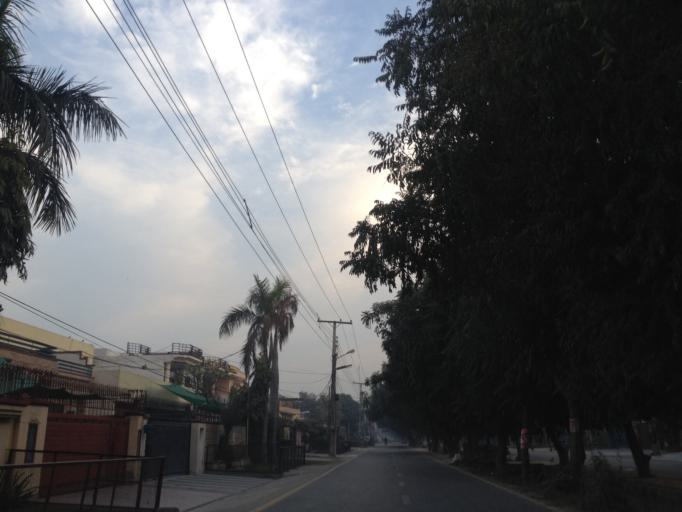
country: PK
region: Punjab
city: Lahore
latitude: 31.4612
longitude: 74.2996
